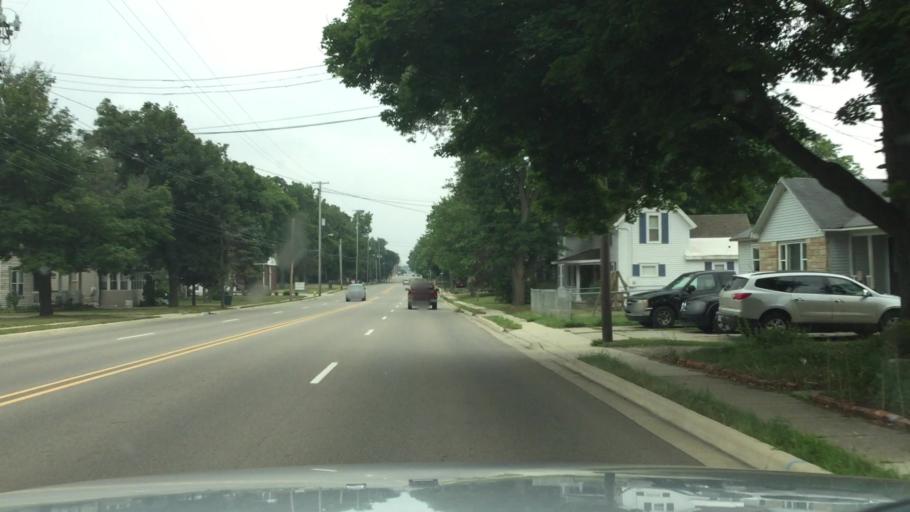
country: US
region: Michigan
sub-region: Shiawassee County
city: Owosso
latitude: 43.0108
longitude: -84.1768
